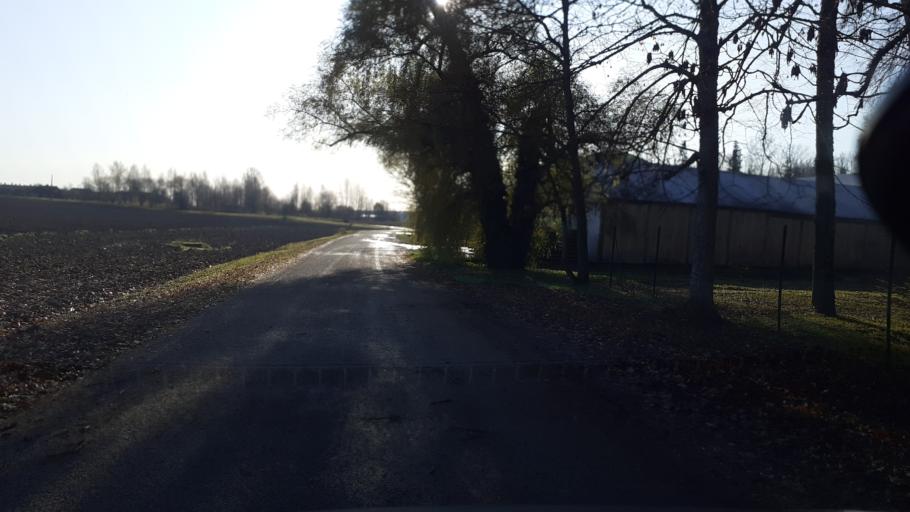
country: LV
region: Kuldigas Rajons
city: Kuldiga
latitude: 56.9996
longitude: 21.8895
